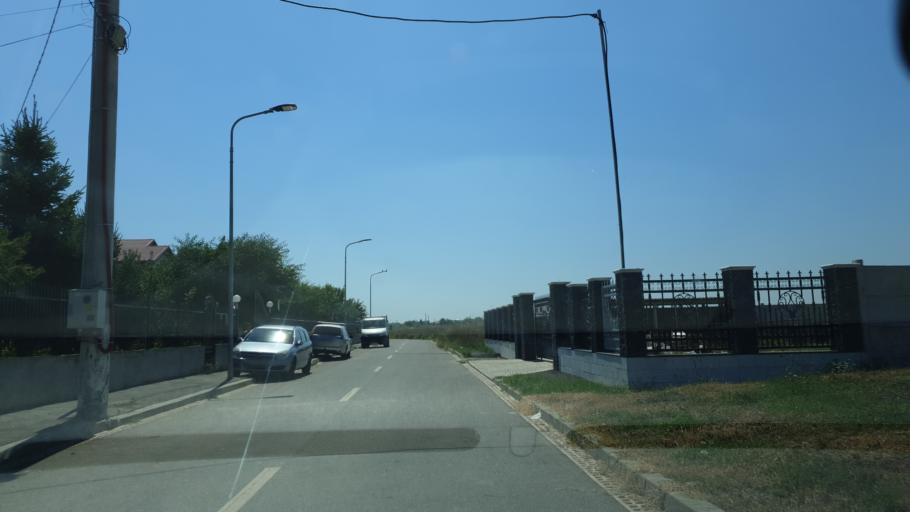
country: RO
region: Ilfov
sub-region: Comuna Chiajna
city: Rosu
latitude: 44.4640
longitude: 26.0208
